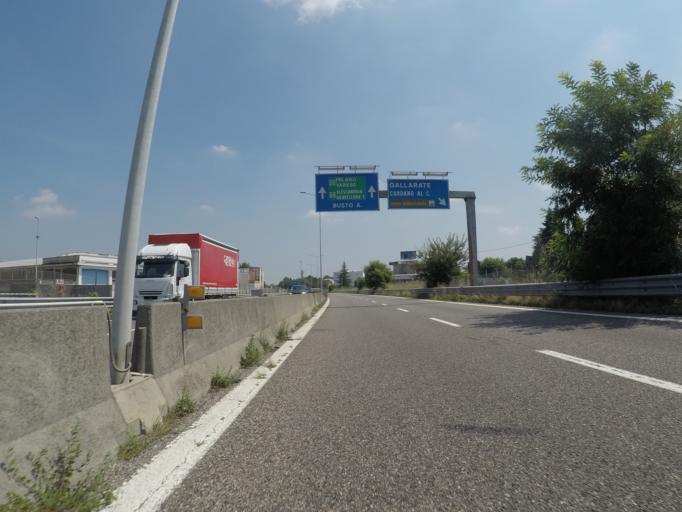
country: IT
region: Lombardy
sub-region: Provincia di Varese
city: Cardano al Campo
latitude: 45.6417
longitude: 8.7782
